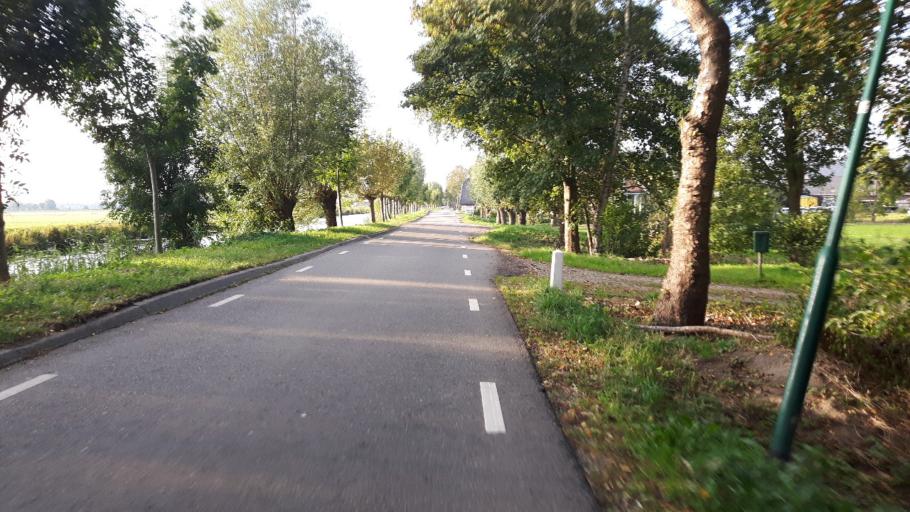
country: NL
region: Utrecht
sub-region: Gemeente Montfoort
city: Montfoort
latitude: 52.0650
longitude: 4.9376
